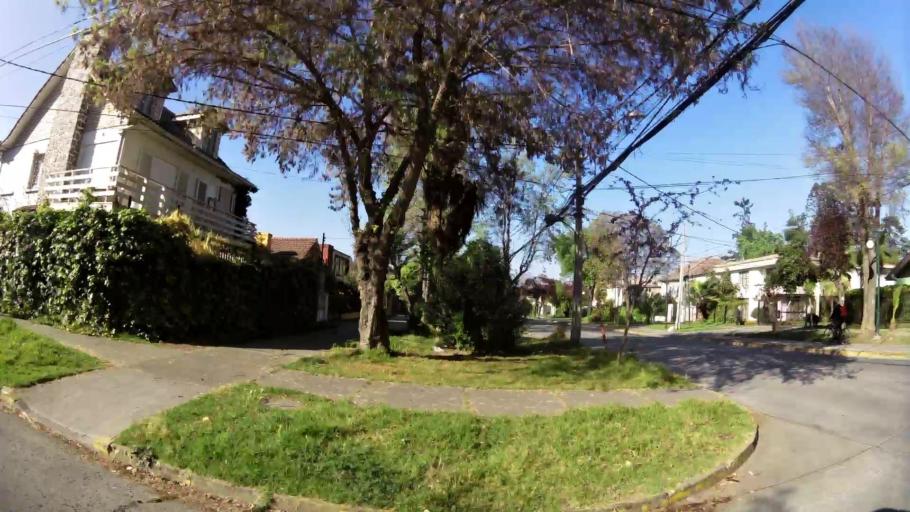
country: CL
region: Santiago Metropolitan
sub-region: Provincia de Santiago
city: Villa Presidente Frei, Nunoa, Santiago, Chile
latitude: -33.4565
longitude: -70.5861
